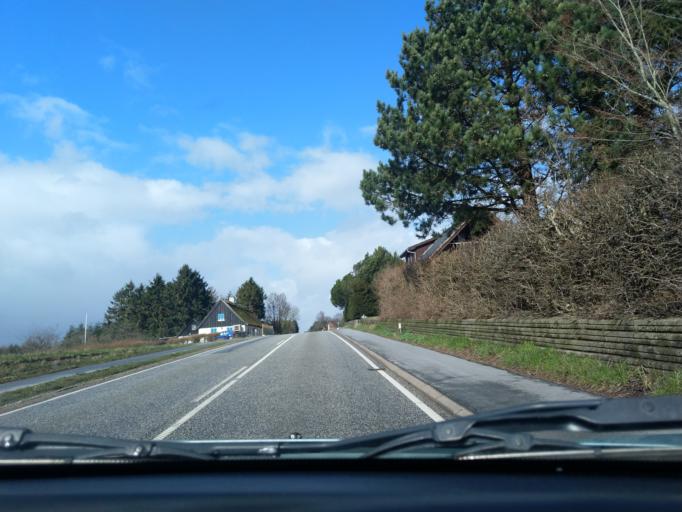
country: DK
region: Zealand
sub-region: Naestved Kommune
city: Naestved
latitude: 55.3051
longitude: 11.6889
